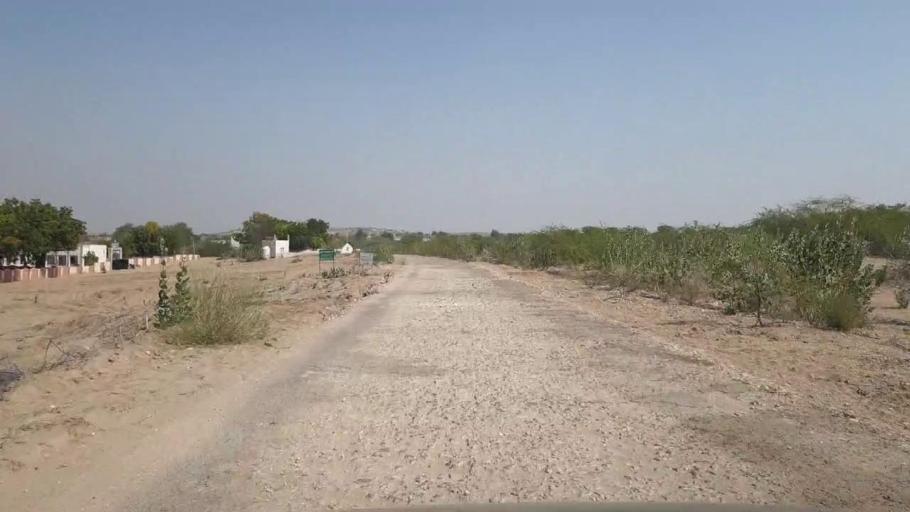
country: PK
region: Sindh
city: Chor
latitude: 25.6964
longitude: 70.1965
